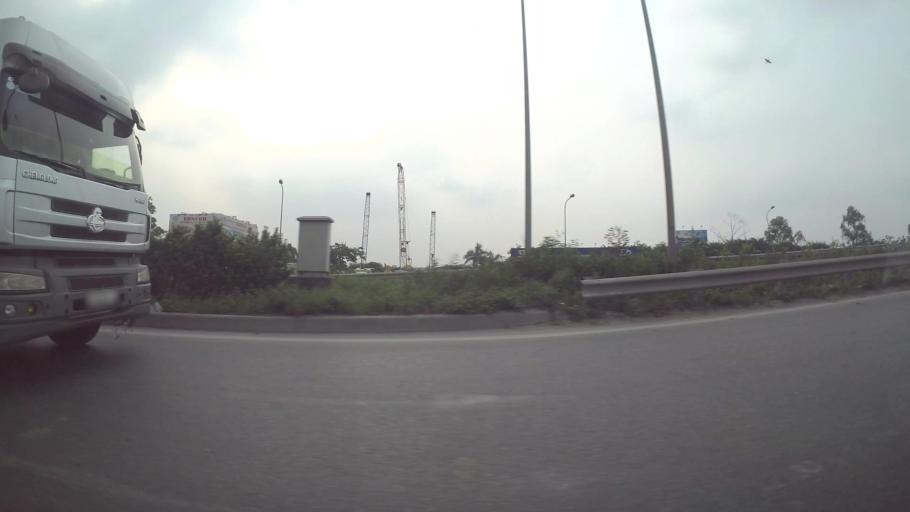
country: VN
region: Ha Noi
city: Trau Quy
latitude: 21.0268
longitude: 105.9287
